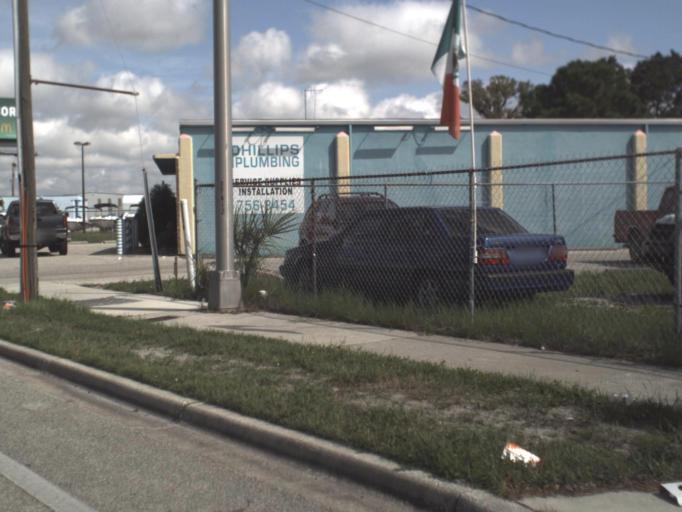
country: US
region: Florida
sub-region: Manatee County
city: Whitfield
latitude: 27.3914
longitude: -82.5604
